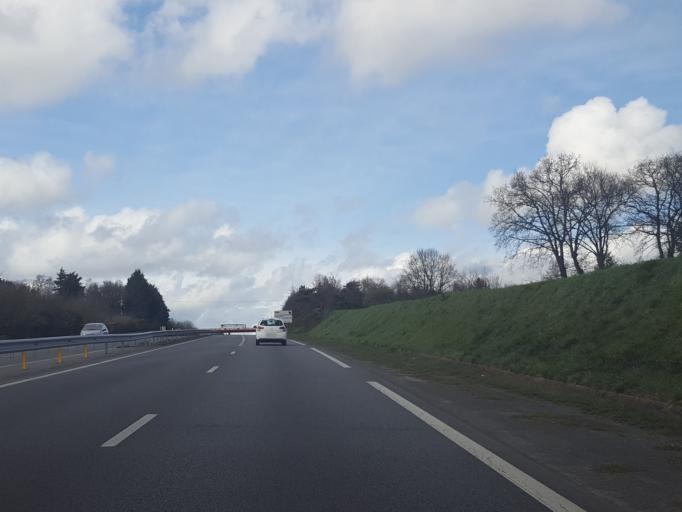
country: FR
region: Brittany
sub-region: Departement d'Ille-et-Vilaine
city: Guichen
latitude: 47.9566
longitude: -1.8161
